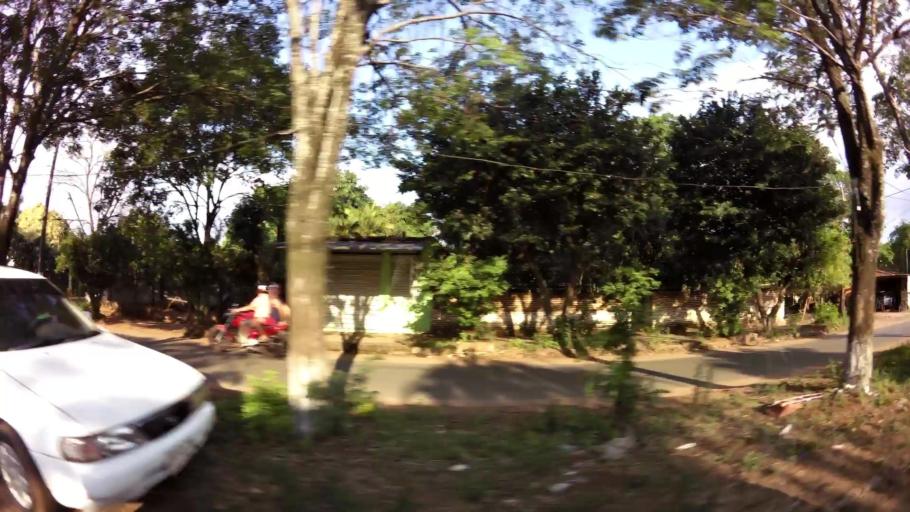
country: PY
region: Central
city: Fernando de la Mora
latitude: -25.3521
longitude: -57.5223
